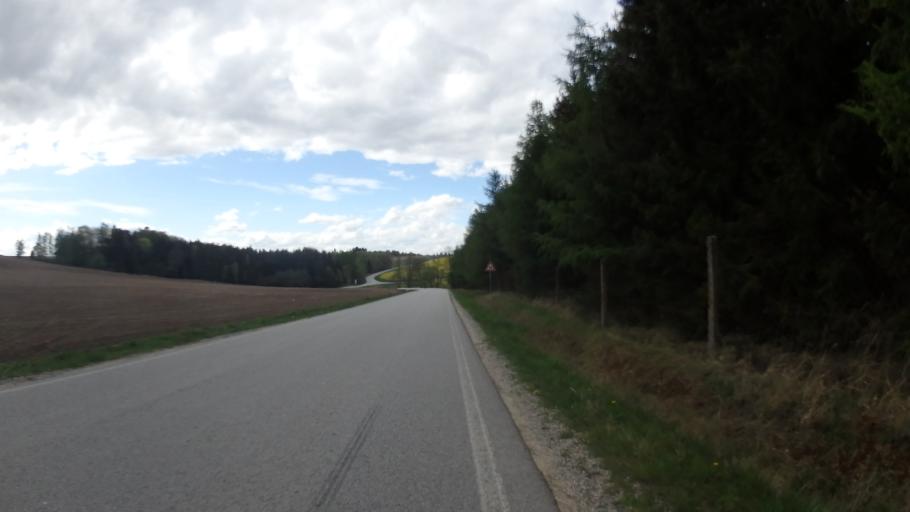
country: CZ
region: Vysocina
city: Merin
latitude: 49.3716
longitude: 15.8949
